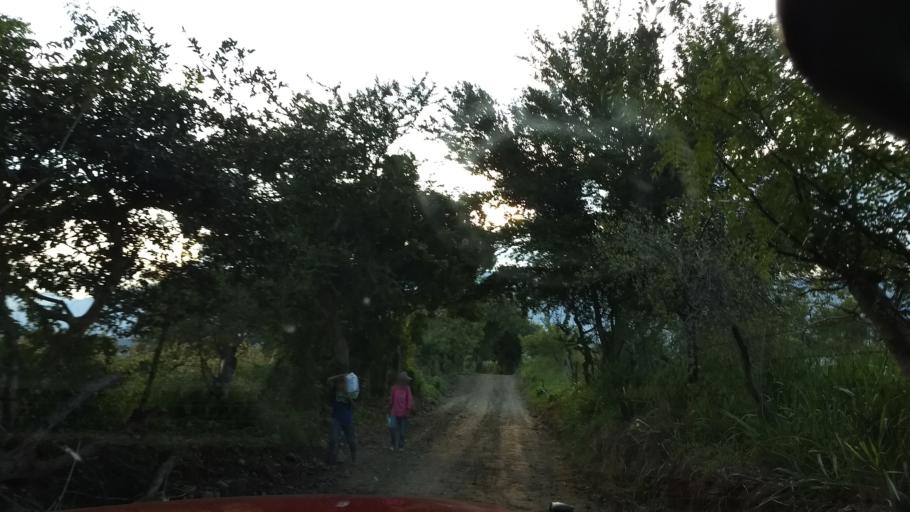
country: MX
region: Jalisco
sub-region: San Gabriel
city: Alista
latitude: 19.5024
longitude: -103.7623
